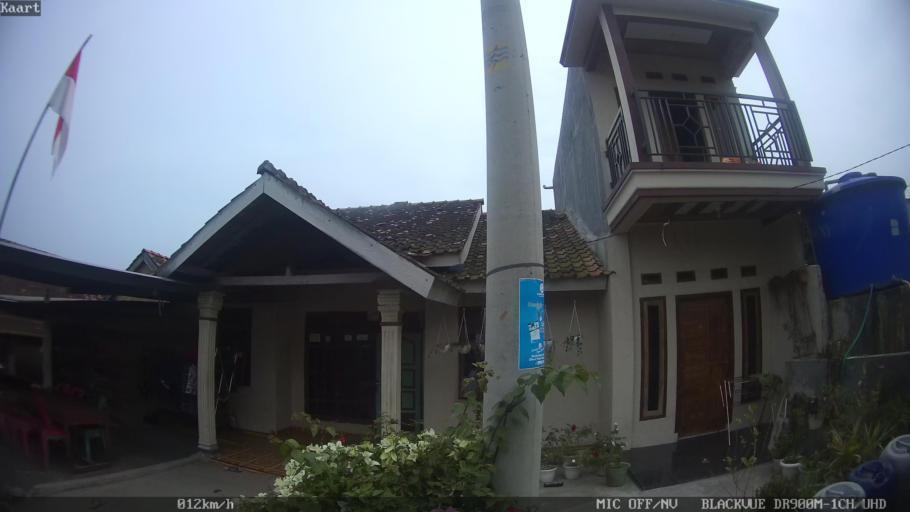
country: ID
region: Lampung
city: Bandarlampung
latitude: -5.4225
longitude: 105.3060
